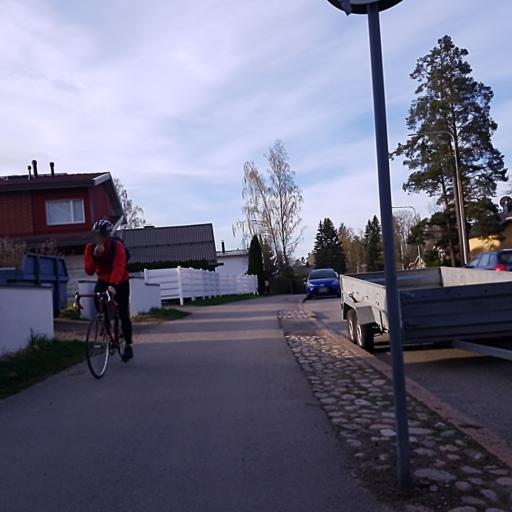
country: FI
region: Uusimaa
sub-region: Helsinki
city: Helsinki
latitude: 60.2522
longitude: 24.9416
